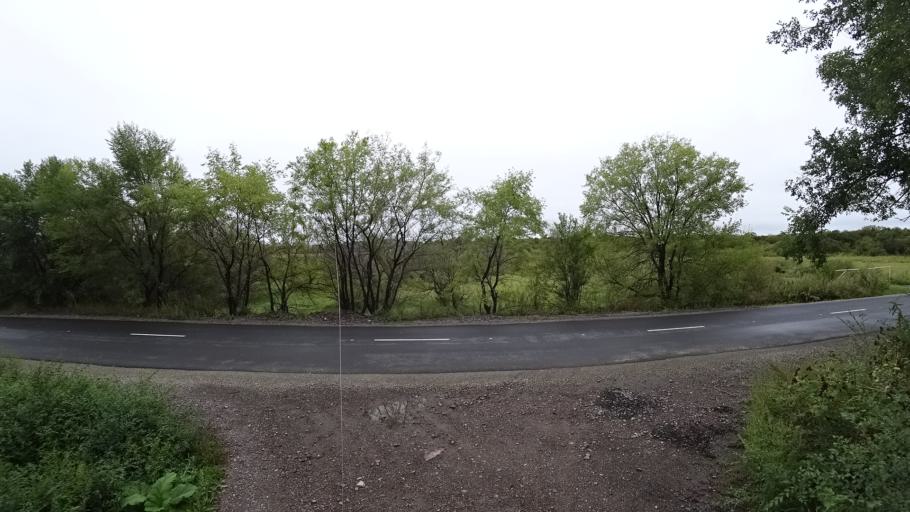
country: RU
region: Primorskiy
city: Monastyrishche
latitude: 44.1997
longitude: 132.4471
